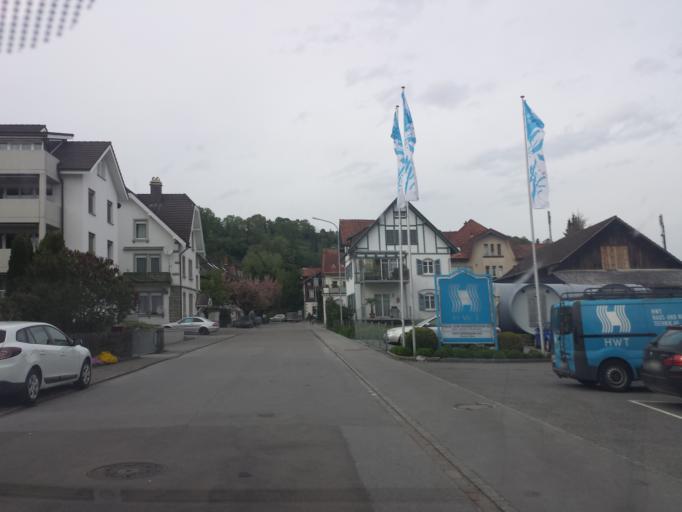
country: CH
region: Saint Gallen
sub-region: Wahlkreis Rheintal
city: Au
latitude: 47.4349
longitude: 9.6402
